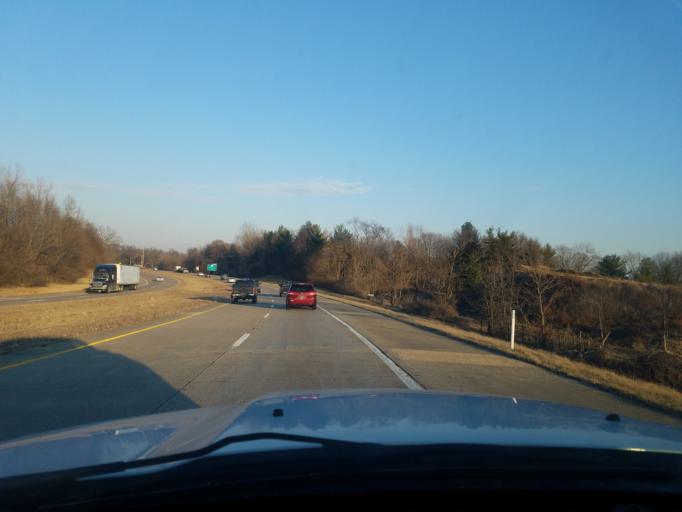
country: US
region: Indiana
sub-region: Warrick County
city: Newburgh
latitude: 37.9495
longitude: -87.4572
